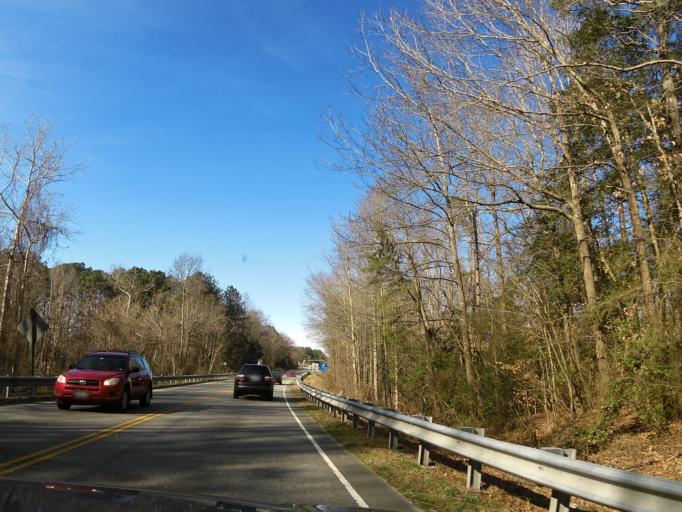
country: US
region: Virginia
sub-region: Isle of Wight County
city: Smithfield
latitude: 36.9741
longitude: -76.6386
